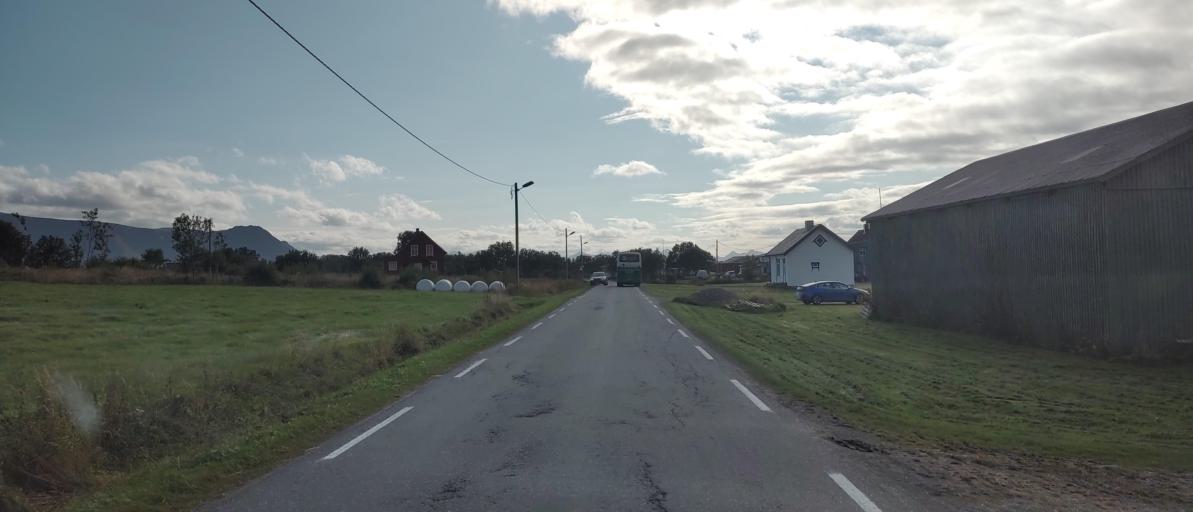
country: NO
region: Nordland
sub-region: Sortland
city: Sortland
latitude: 69.0486
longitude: 15.5202
